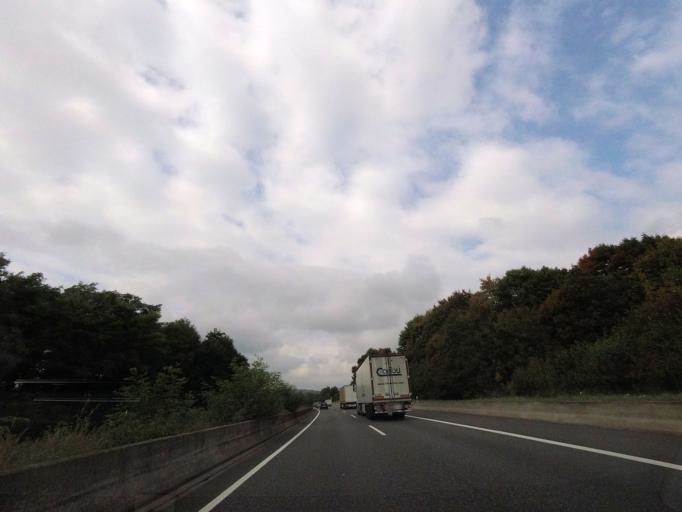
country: DE
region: Thuringia
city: Dankmarshausen
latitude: 50.9598
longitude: 10.0235
